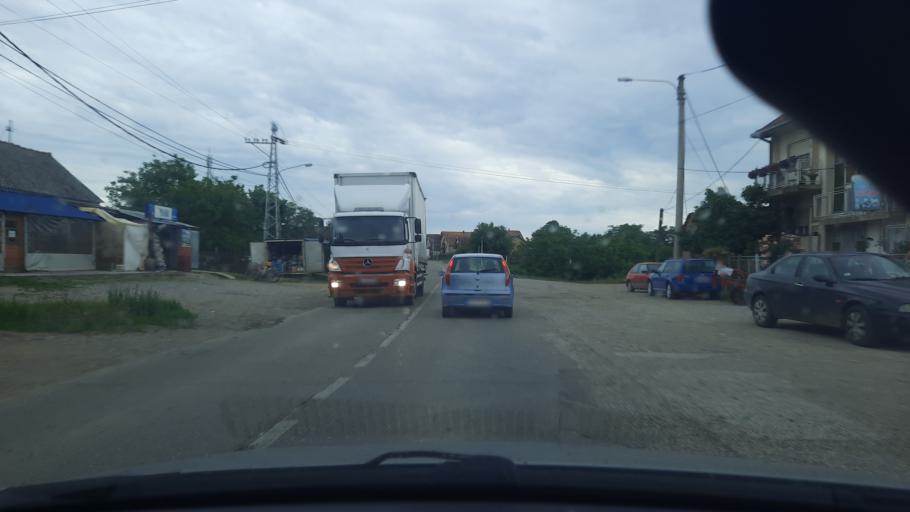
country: RS
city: Jevremovac
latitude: 44.7210
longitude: 19.6633
